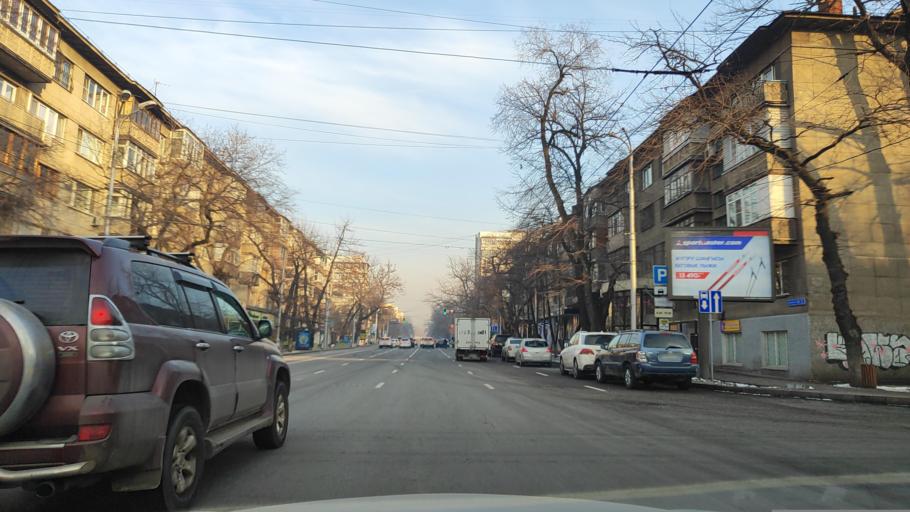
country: KZ
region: Almaty Qalasy
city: Almaty
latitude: 43.2503
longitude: 76.9542
